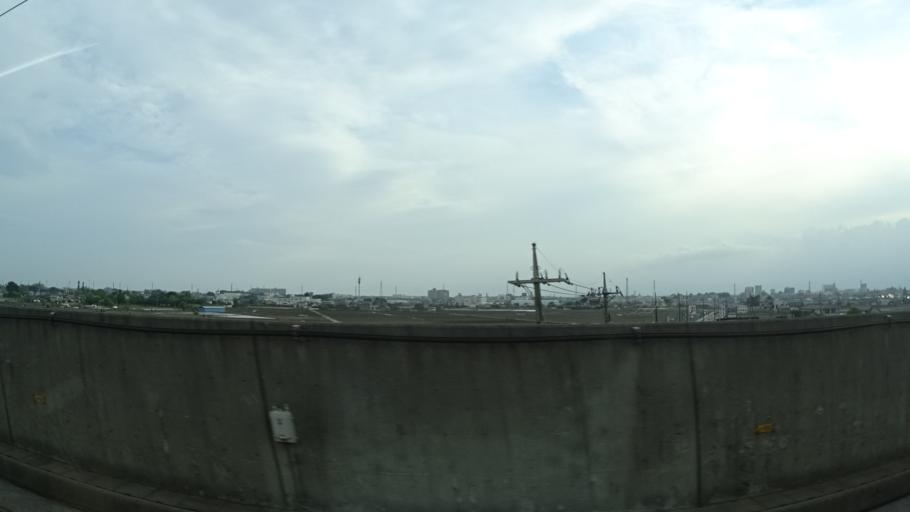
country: JP
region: Saitama
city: Konosu
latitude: 36.0634
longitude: 139.5370
